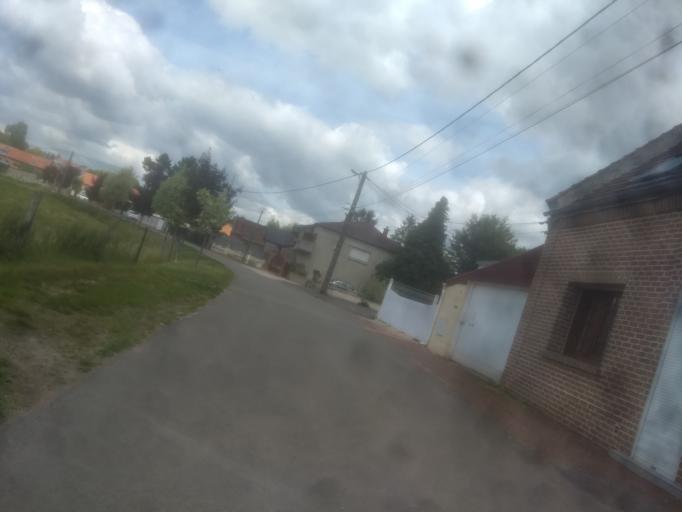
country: FR
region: Nord-Pas-de-Calais
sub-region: Departement du Pas-de-Calais
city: Maroeuil
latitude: 50.3205
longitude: 2.7068
